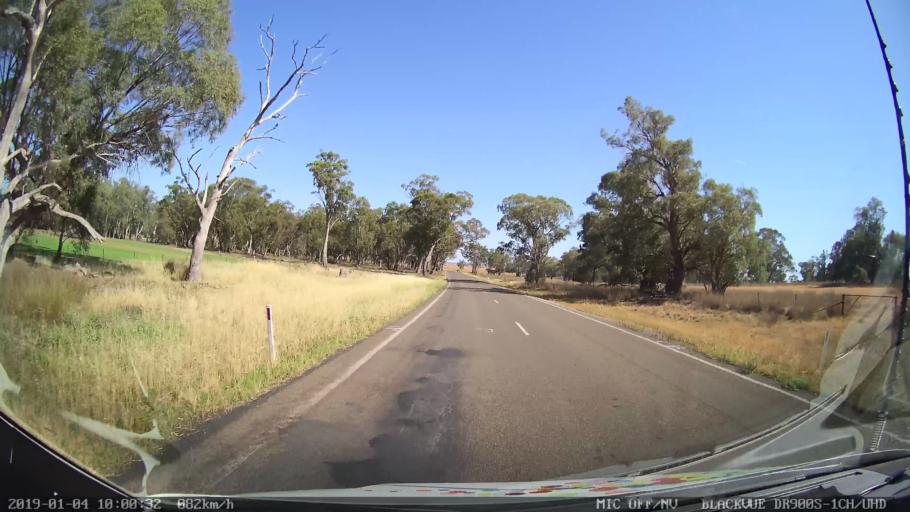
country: AU
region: New South Wales
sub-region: Cabonne
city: Canowindra
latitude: -33.4966
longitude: 148.3784
